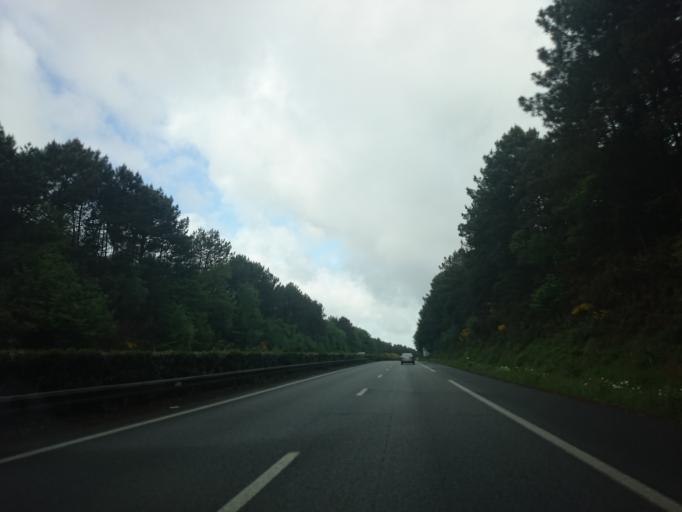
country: FR
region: Brittany
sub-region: Departement du Morbihan
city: Saint-Nolff
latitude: 47.6721
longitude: -2.6943
